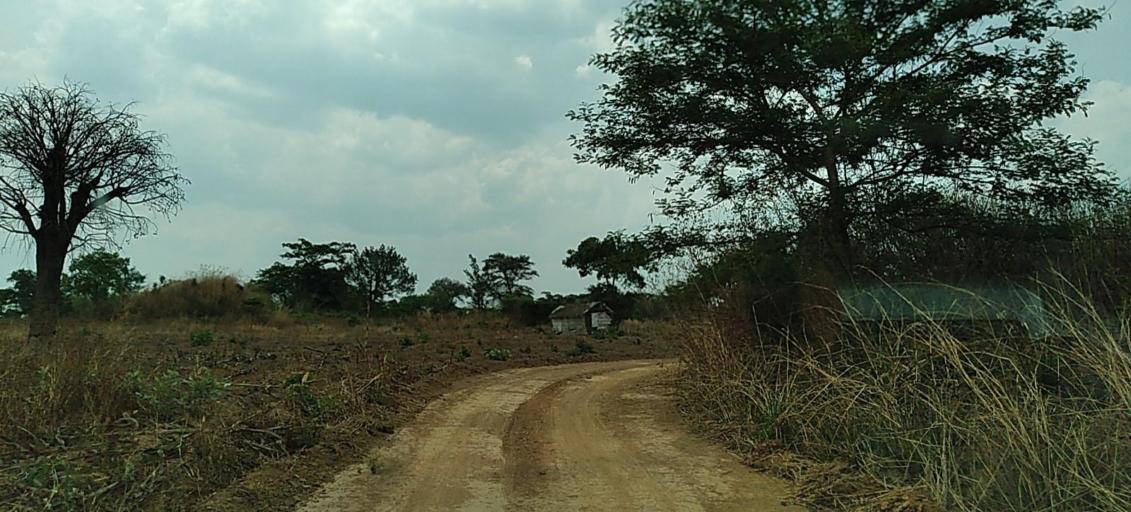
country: ZM
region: Copperbelt
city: Chililabombwe
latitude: -12.3527
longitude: 27.8010
